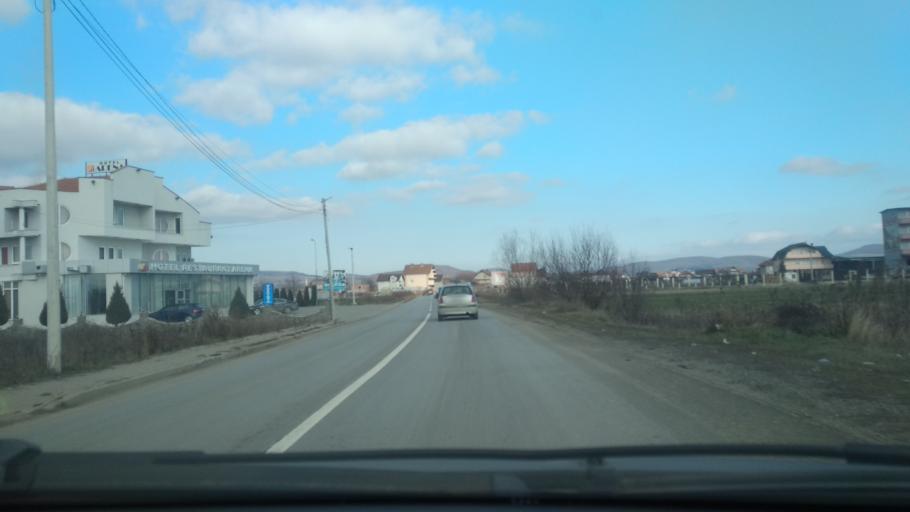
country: XK
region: Pristina
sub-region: Komuna e Obiliqit
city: Obiliq
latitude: 42.7297
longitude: 21.1023
